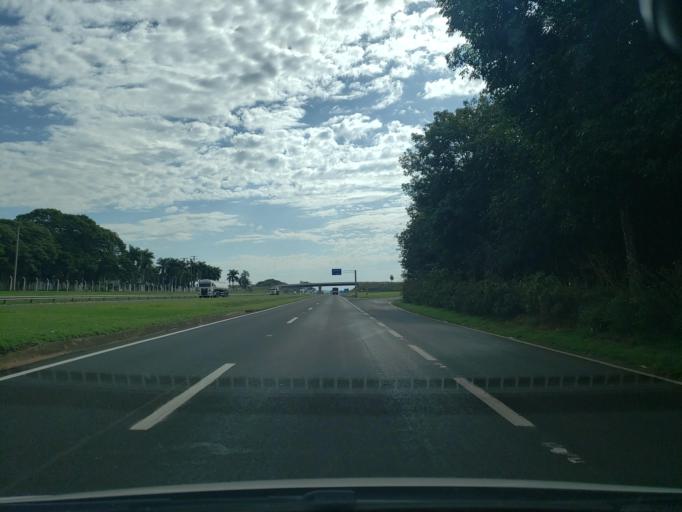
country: BR
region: Sao Paulo
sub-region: Promissao
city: Promissao
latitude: -21.6330
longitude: -49.8369
